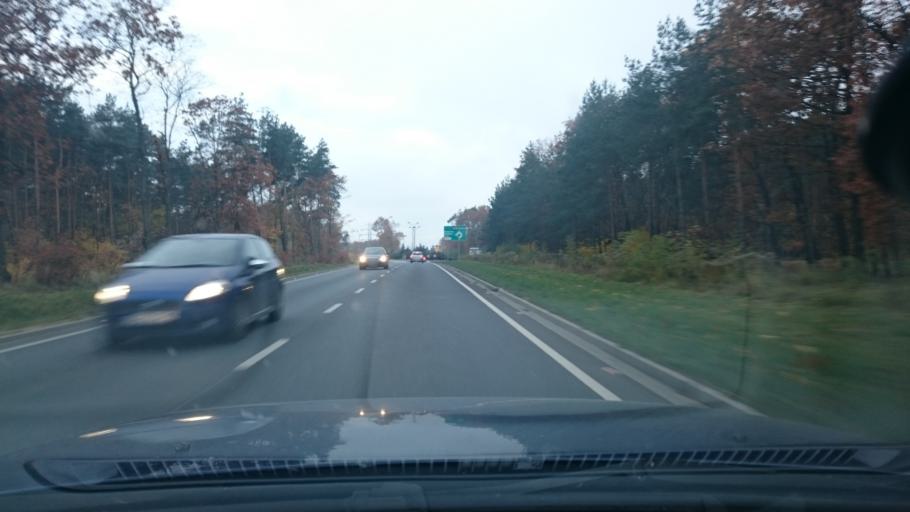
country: PL
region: Silesian Voivodeship
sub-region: Rybnik
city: Rybnik
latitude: 50.1136
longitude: 18.5564
